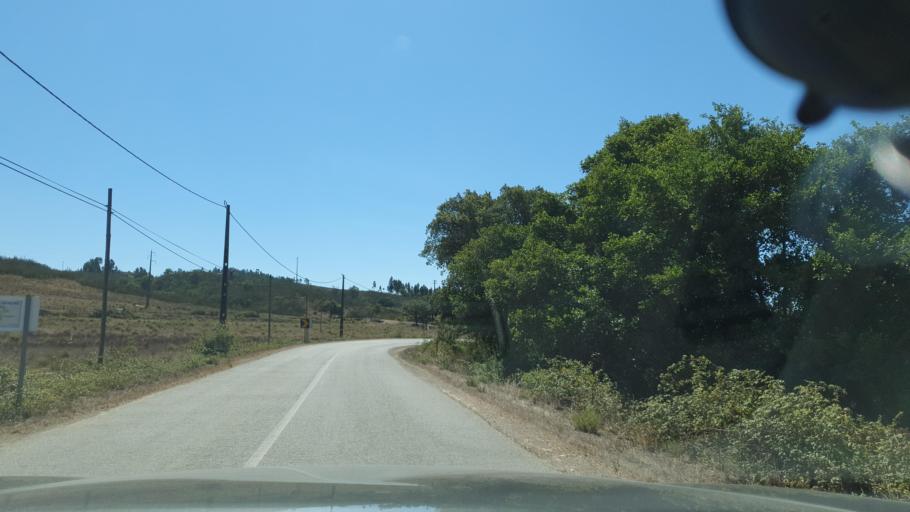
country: PT
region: Beja
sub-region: Odemira
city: Sao Teotonio
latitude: 37.4867
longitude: -8.6358
